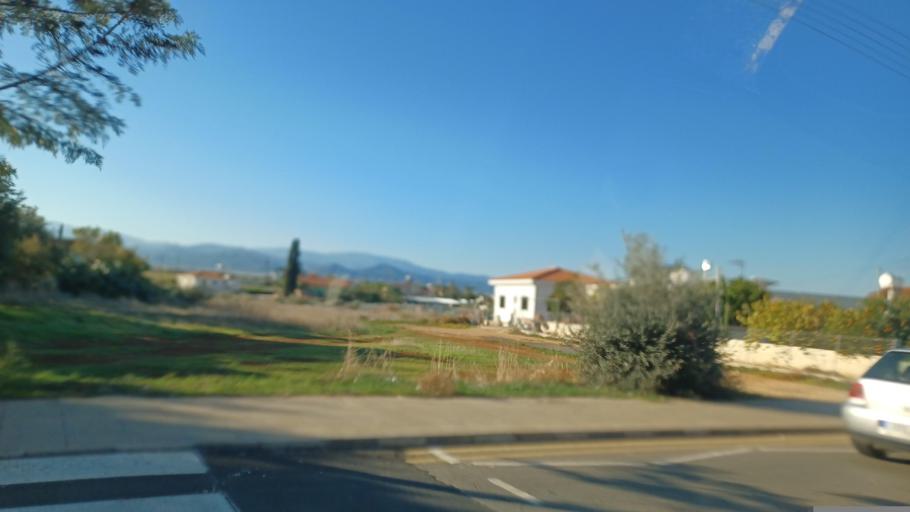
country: CY
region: Lefkosia
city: Astromeritis
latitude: 35.1396
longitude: 33.0470
